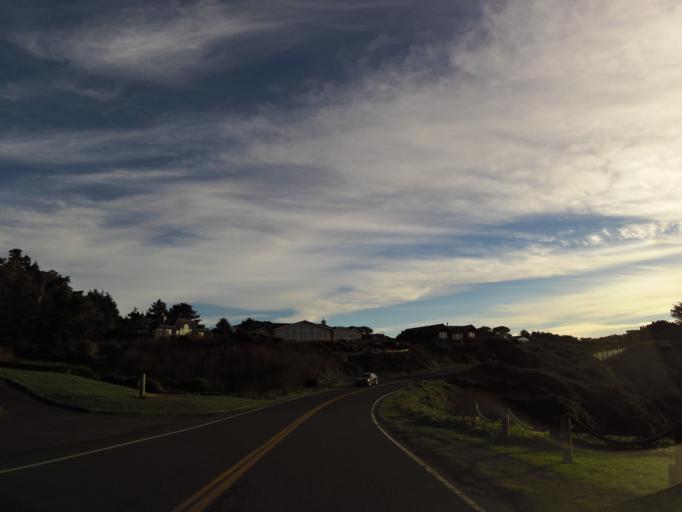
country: US
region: California
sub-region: Mendocino County
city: Fort Bragg
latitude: 39.3159
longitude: -123.7998
